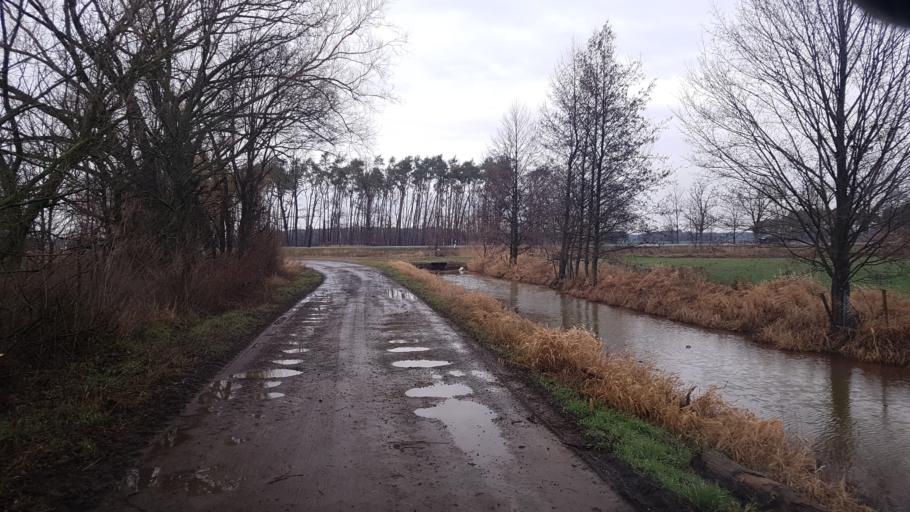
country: DE
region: Brandenburg
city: Bad Liebenwerda
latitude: 51.5272
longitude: 13.3252
